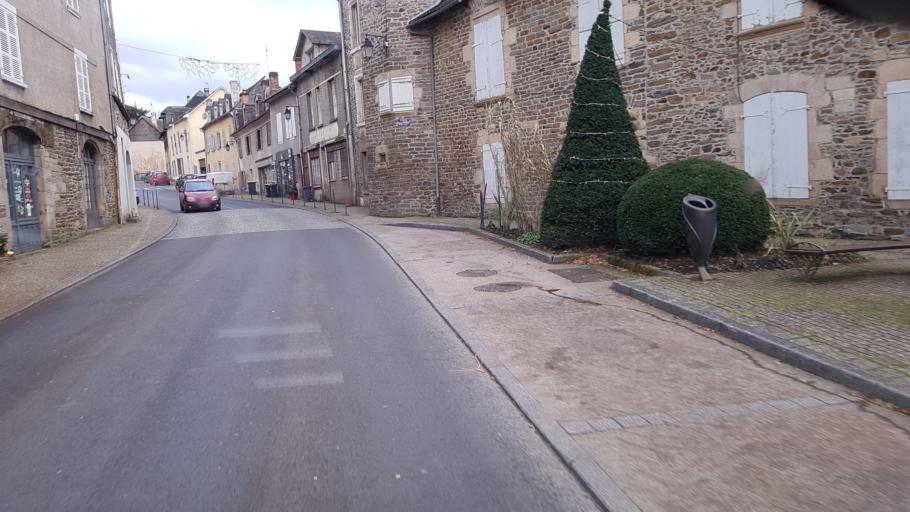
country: FR
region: Limousin
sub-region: Departement de la Correze
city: Uzerche
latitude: 45.4226
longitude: 1.5632
